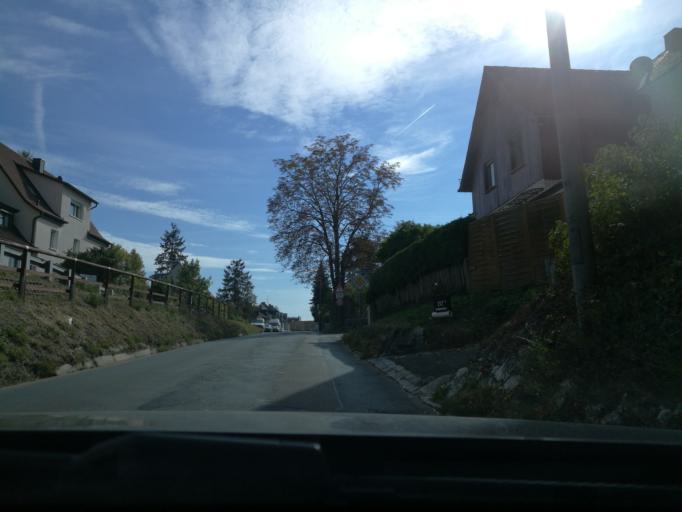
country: DE
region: Bavaria
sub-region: Regierungsbezirk Mittelfranken
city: Furth
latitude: 49.4973
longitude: 10.9711
